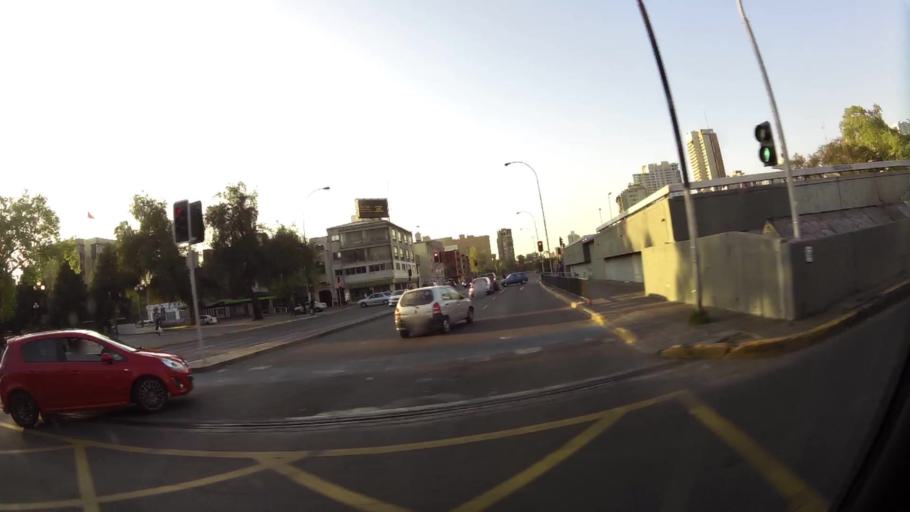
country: CL
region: Santiago Metropolitan
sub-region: Provincia de Santiago
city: Santiago
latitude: -33.4465
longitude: -70.6605
